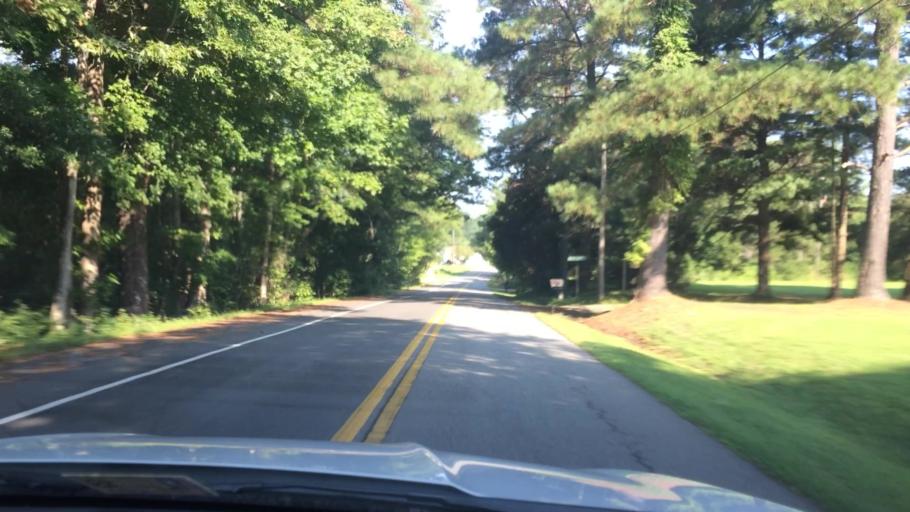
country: US
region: Virginia
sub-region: King William County
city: West Point
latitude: 37.5649
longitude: -76.8004
